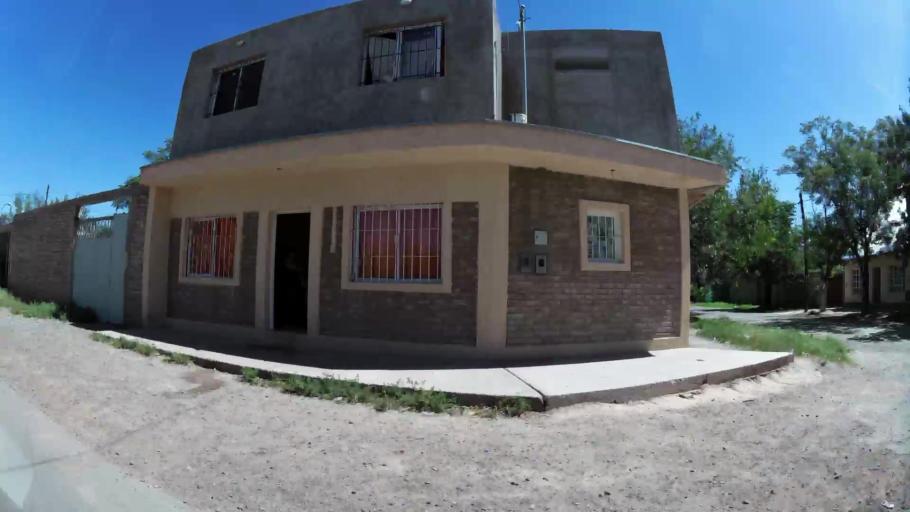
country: AR
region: Mendoza
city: Las Heras
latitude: -32.8657
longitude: -68.7967
